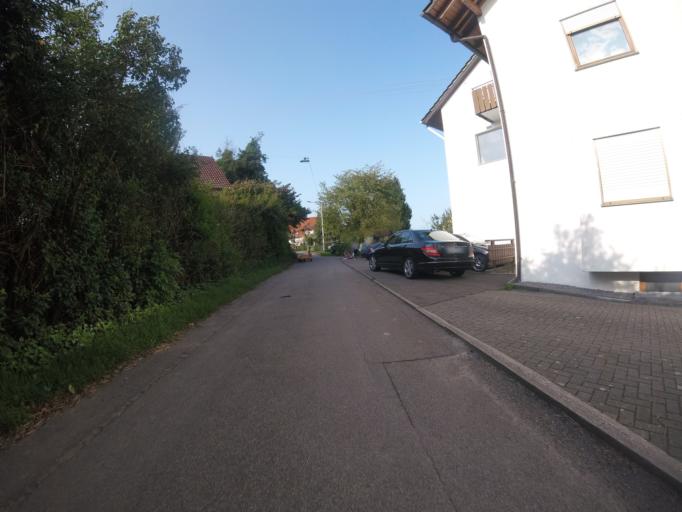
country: DE
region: Baden-Wuerttemberg
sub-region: Regierungsbezirk Stuttgart
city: Backnang
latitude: 48.9696
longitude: 9.4360
